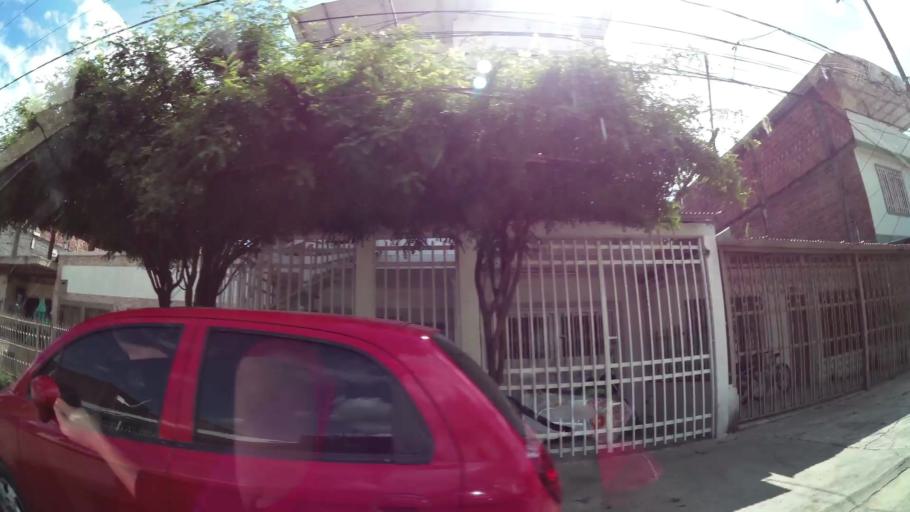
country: CO
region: Valle del Cauca
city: Cali
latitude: 3.4037
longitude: -76.5139
